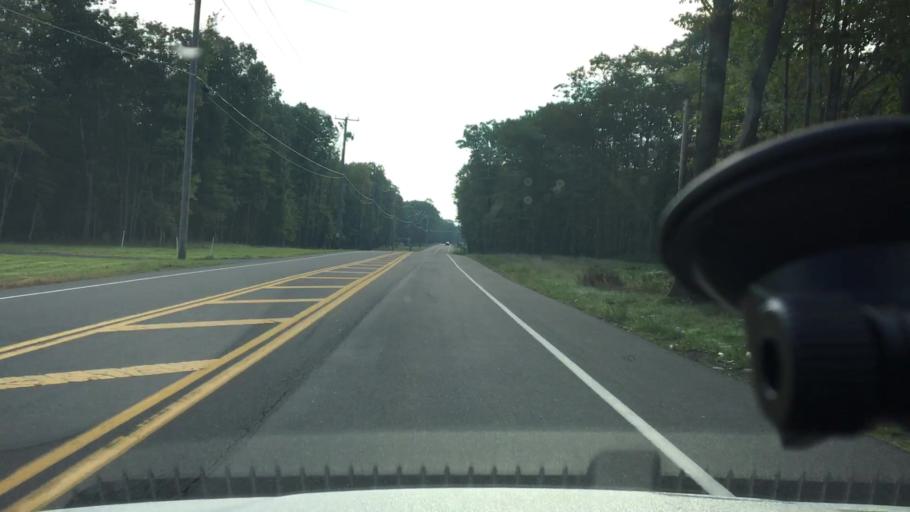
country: US
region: Pennsylvania
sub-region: Monroe County
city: Mount Pocono
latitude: 41.1050
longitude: -75.3805
